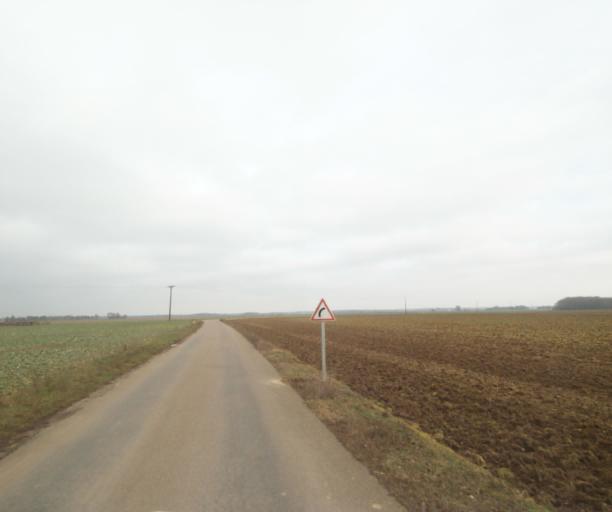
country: FR
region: Champagne-Ardenne
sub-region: Departement de la Haute-Marne
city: Villiers-en-Lieu
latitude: 48.6683
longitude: 4.8355
